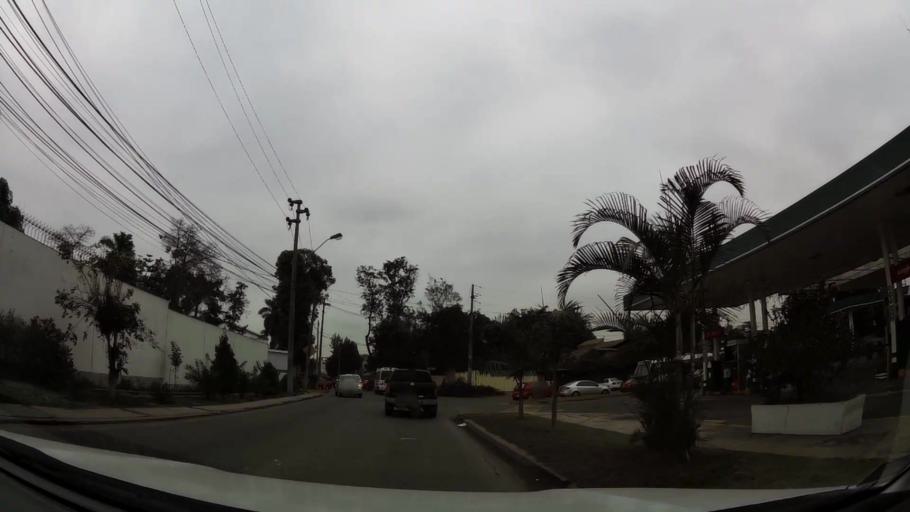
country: PE
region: Lima
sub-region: Lima
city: La Molina
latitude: -12.0753
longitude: -76.9368
